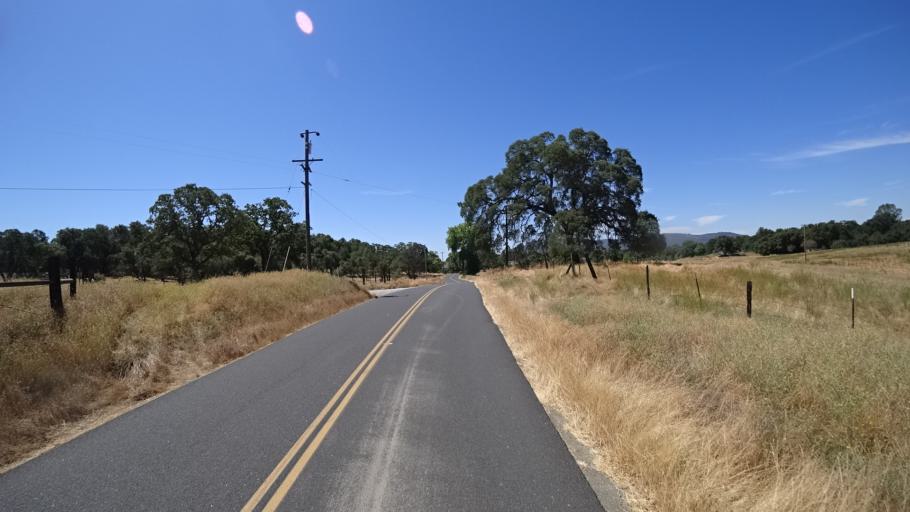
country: US
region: California
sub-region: Calaveras County
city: Angels Camp
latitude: 38.0898
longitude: -120.5563
